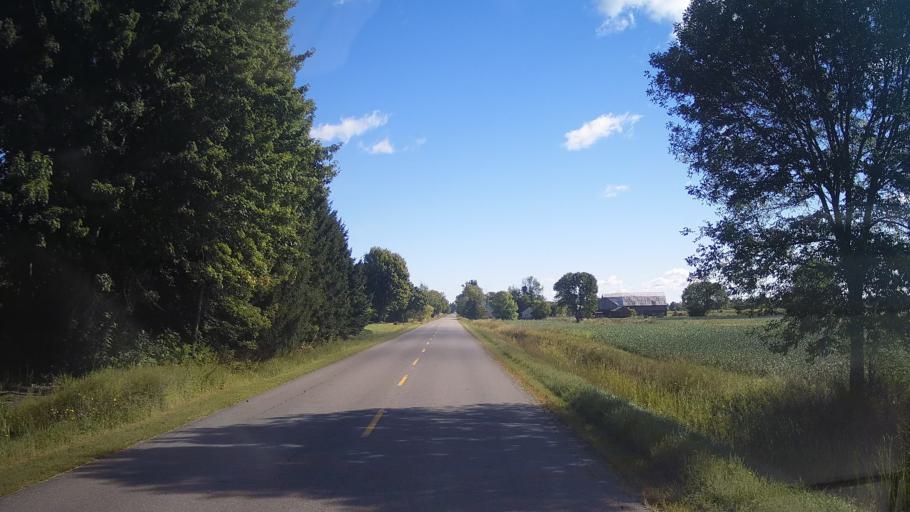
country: CA
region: Ontario
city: Prescott
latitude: 44.9059
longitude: -75.3891
